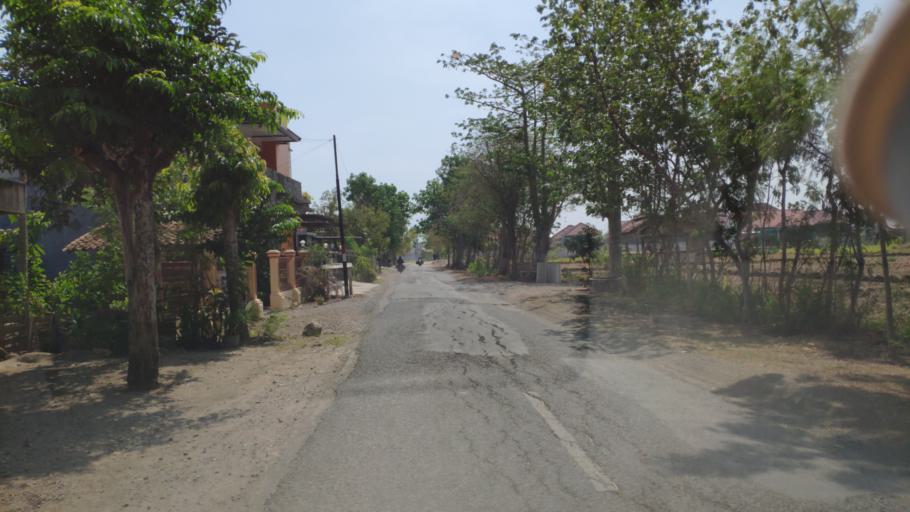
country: ID
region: Central Java
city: Bangkle
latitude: -6.9812
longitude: 111.4330
